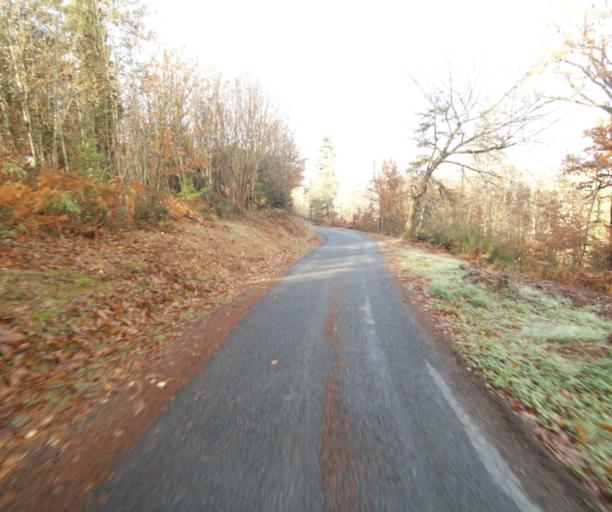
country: FR
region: Limousin
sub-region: Departement de la Correze
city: Chameyrat
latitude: 45.2259
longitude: 1.7340
